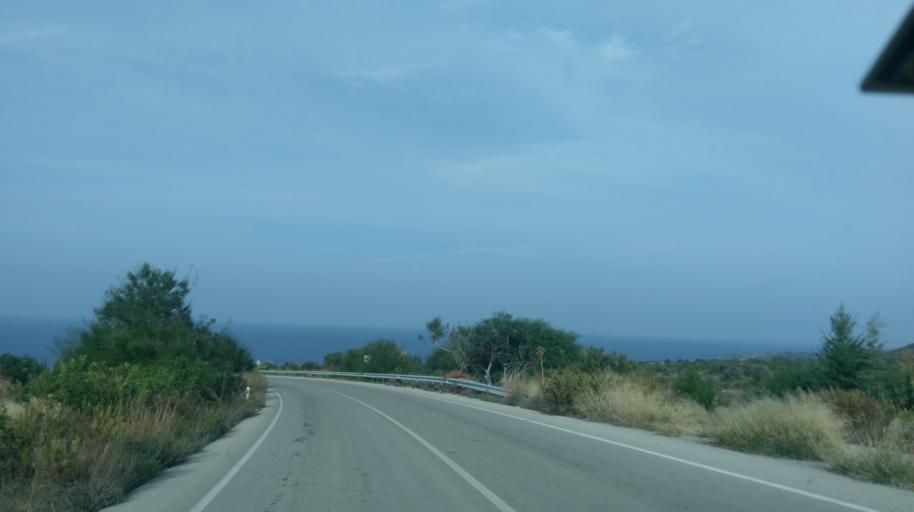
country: CY
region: Ammochostos
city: Trikomo
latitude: 35.4327
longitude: 33.9619
